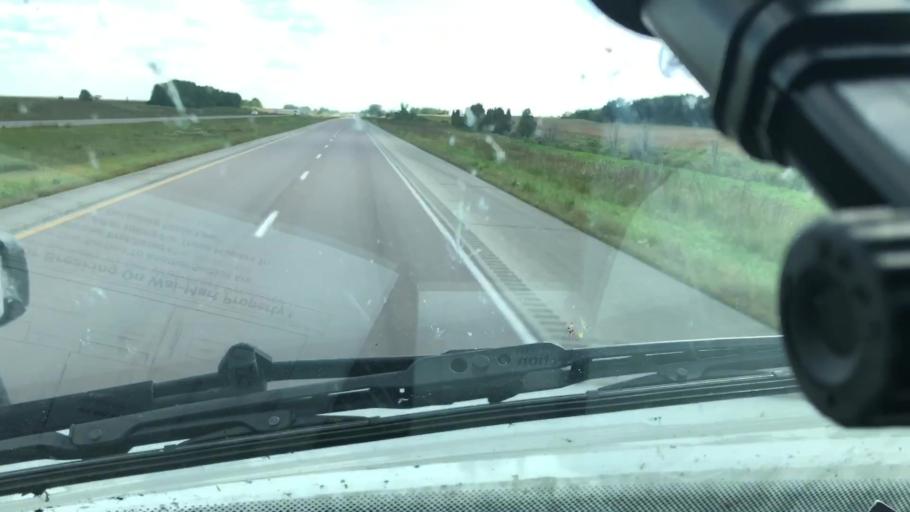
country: US
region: Iowa
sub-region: Worth County
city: Manly
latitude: 43.3167
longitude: -93.3489
